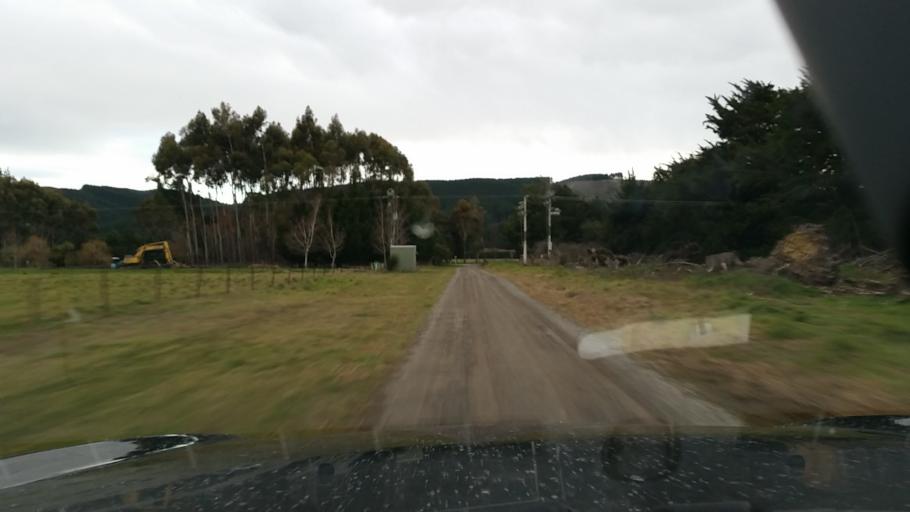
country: NZ
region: Nelson
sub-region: Nelson City
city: Nelson
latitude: -41.5648
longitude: 173.5238
